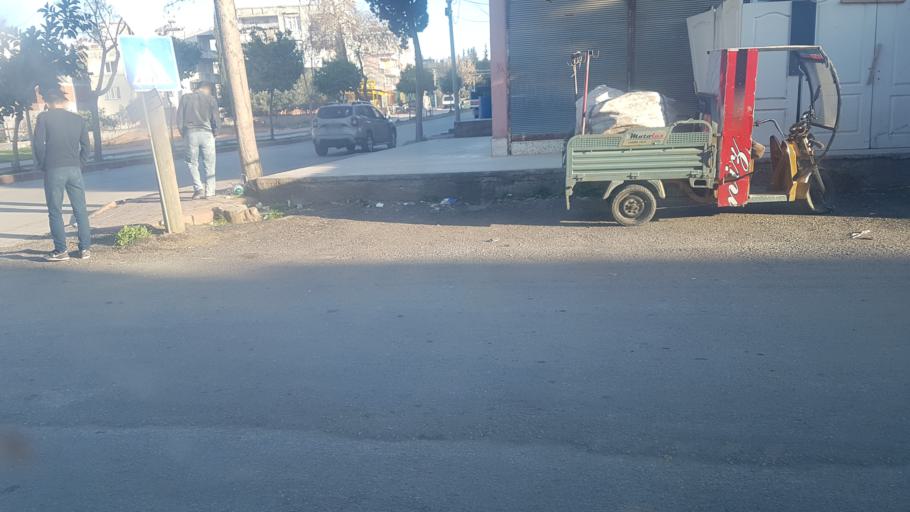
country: TR
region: Adana
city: Seyhan
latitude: 37.0230
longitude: 35.2710
